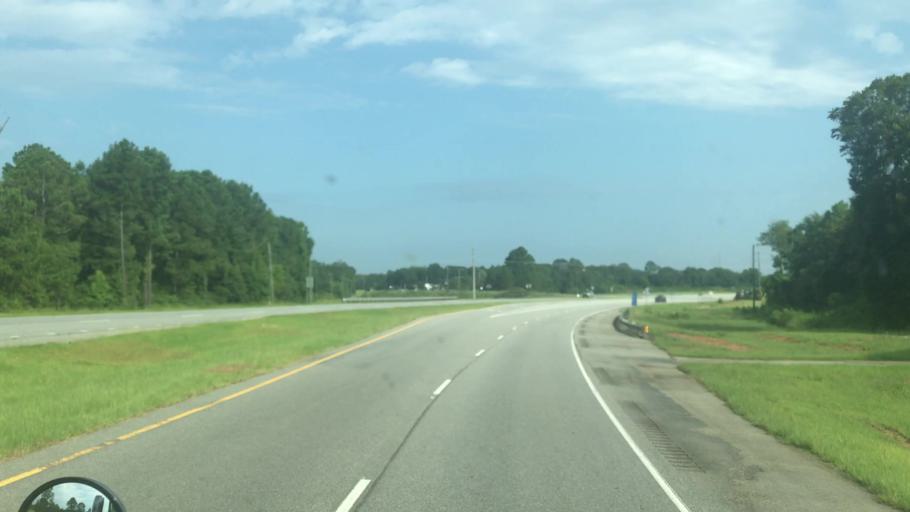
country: US
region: Georgia
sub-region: Early County
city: Blakely
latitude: 31.3555
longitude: -84.9219
